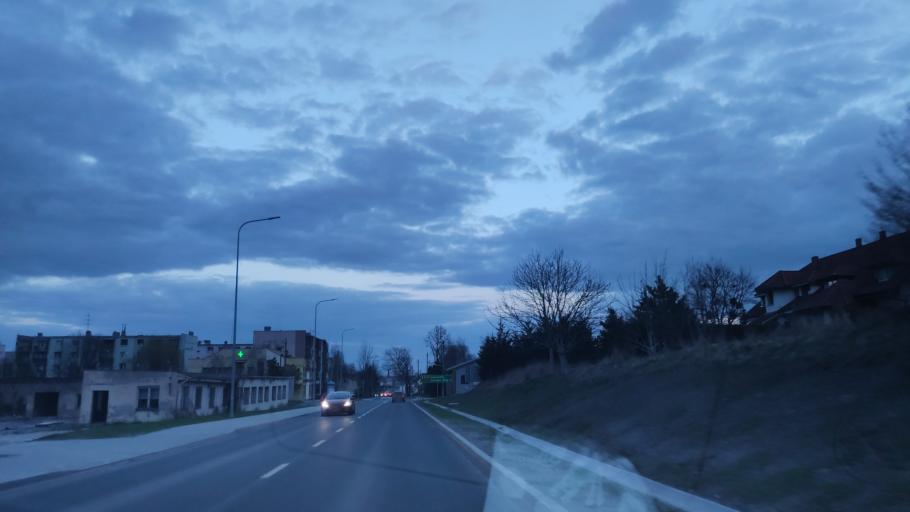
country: PL
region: Kujawsko-Pomorskie
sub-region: Powiat zninski
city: Znin
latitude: 52.8495
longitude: 17.7115
